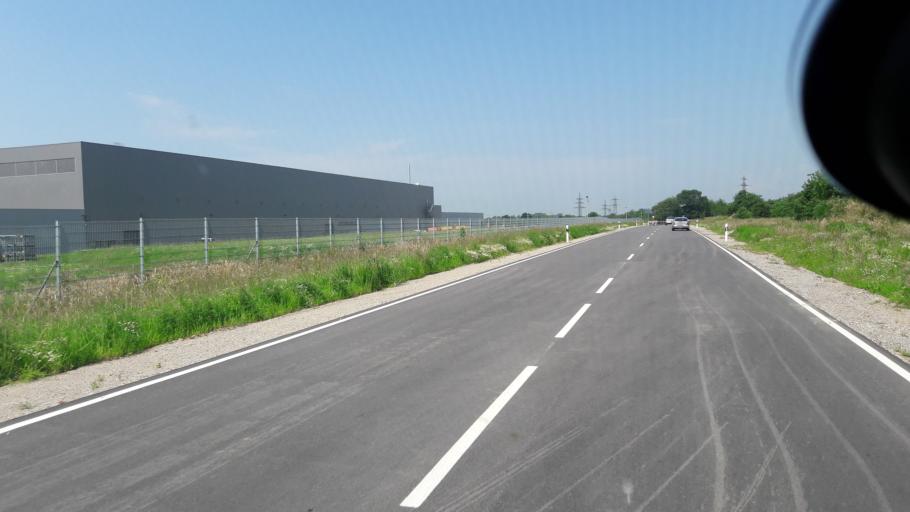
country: DE
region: Baden-Wuerttemberg
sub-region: Karlsruhe Region
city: Kuppenheim
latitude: 48.8418
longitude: 8.2555
